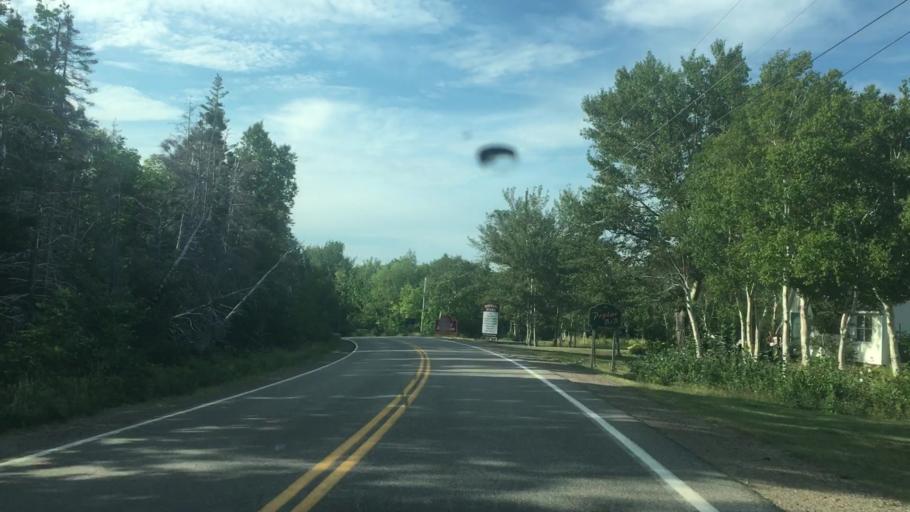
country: CA
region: Nova Scotia
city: Sydney Mines
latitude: 46.8203
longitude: -60.7964
